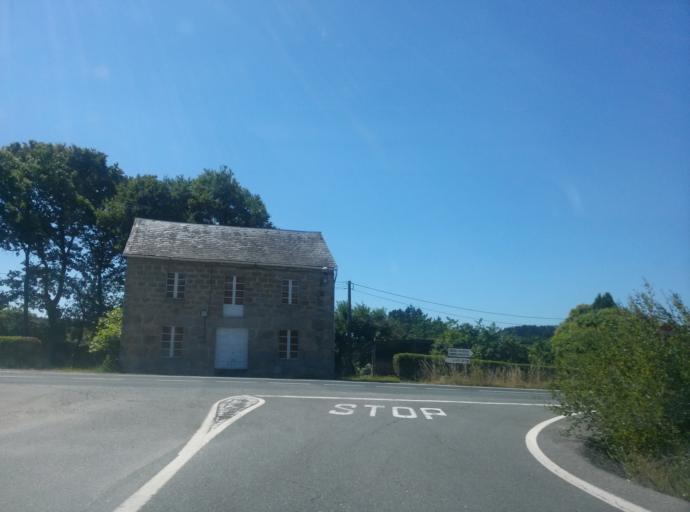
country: ES
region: Galicia
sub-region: Provincia de Lugo
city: Mos
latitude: 43.0952
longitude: -7.4778
